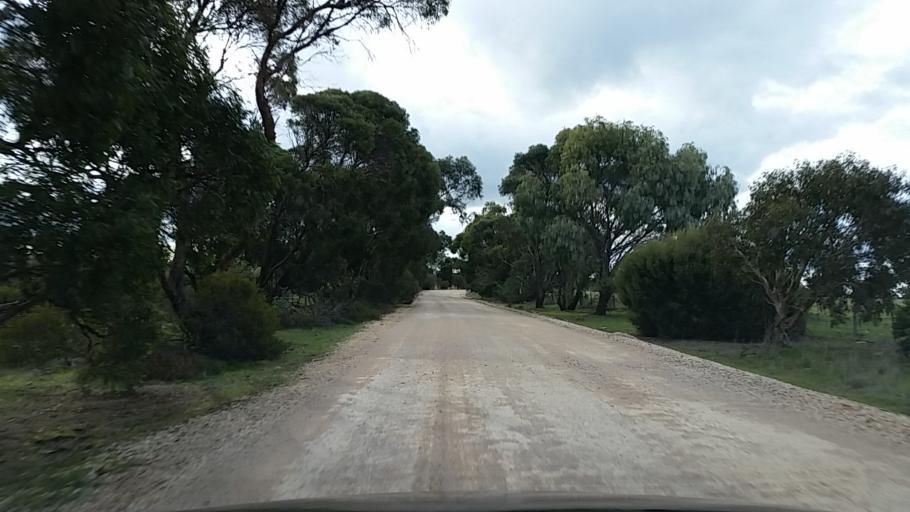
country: AU
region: South Australia
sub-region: Mount Barker
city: Callington
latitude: -34.9955
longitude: 139.0575
